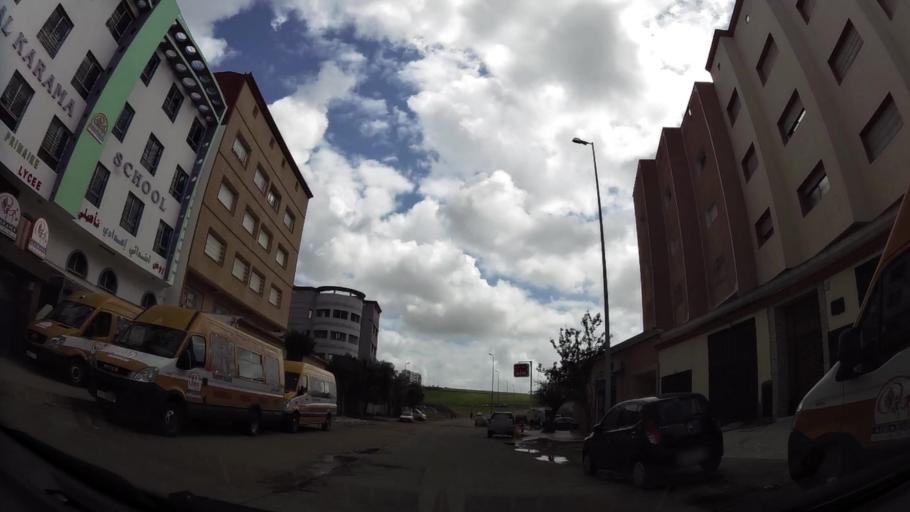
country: MA
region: Grand Casablanca
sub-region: Casablanca
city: Casablanca
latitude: 33.5295
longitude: -7.6019
